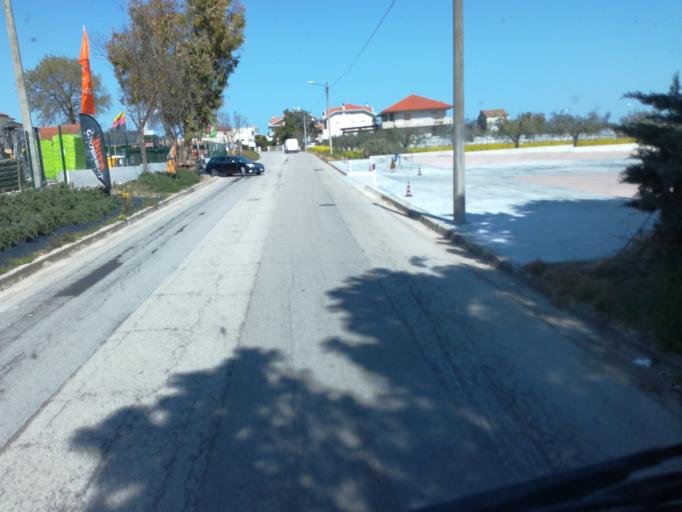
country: IT
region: Abruzzo
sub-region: Provincia di Chieti
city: Francavilla al Mare
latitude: 42.3960
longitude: 14.2954
